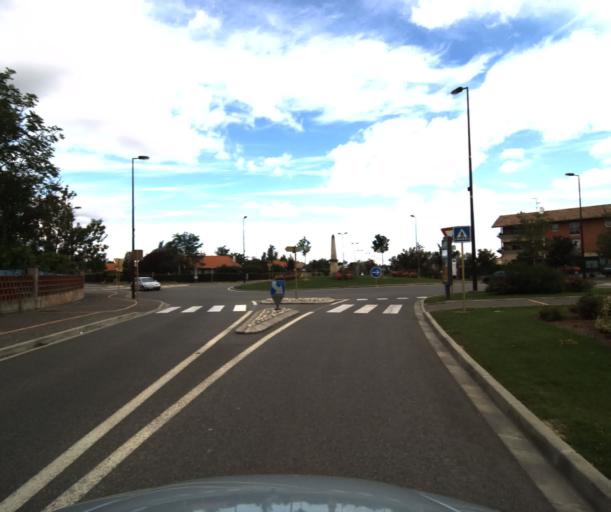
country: FR
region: Midi-Pyrenees
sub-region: Departement de la Haute-Garonne
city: Muret
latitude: 43.4680
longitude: 1.3240
